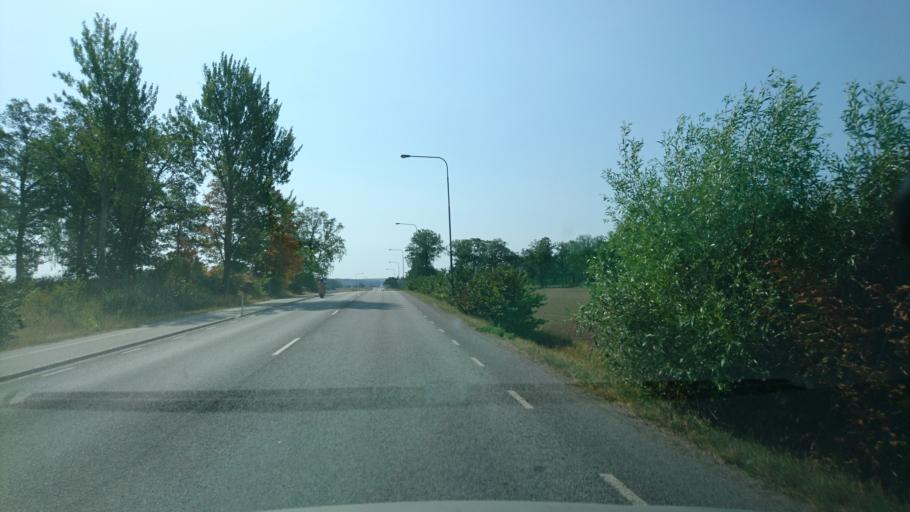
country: SE
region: Uppsala
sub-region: Uppsala Kommun
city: Uppsala
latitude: 59.8257
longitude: 17.6450
